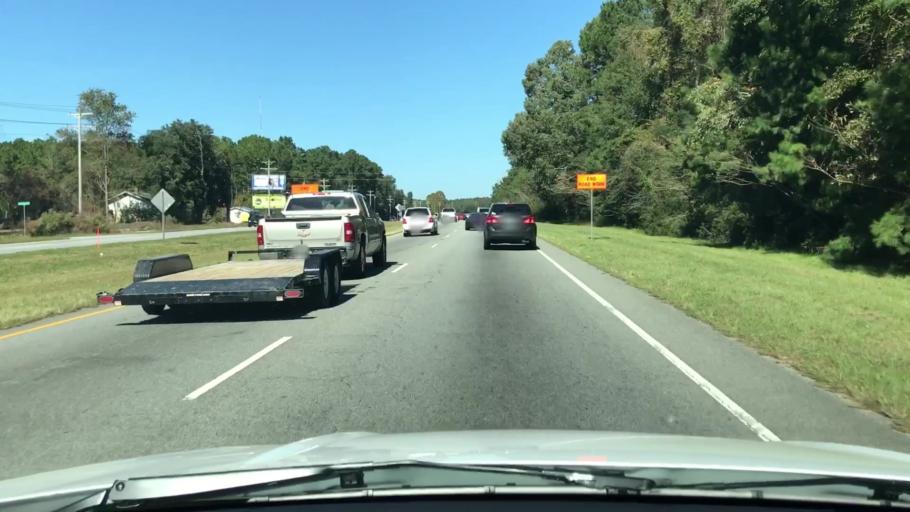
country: US
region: South Carolina
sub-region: Beaufort County
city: Bluffton
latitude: 32.3141
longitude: -80.9345
